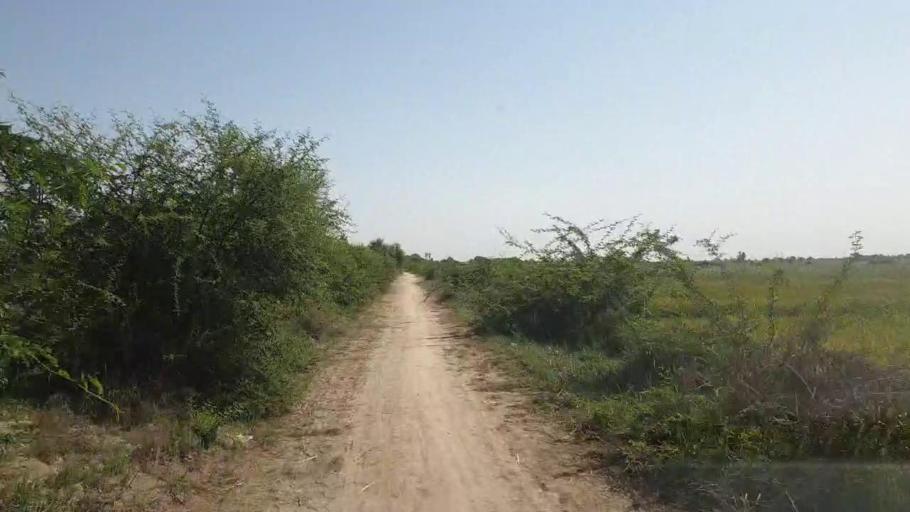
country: PK
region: Sindh
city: Kadhan
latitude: 24.6064
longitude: 69.0018
